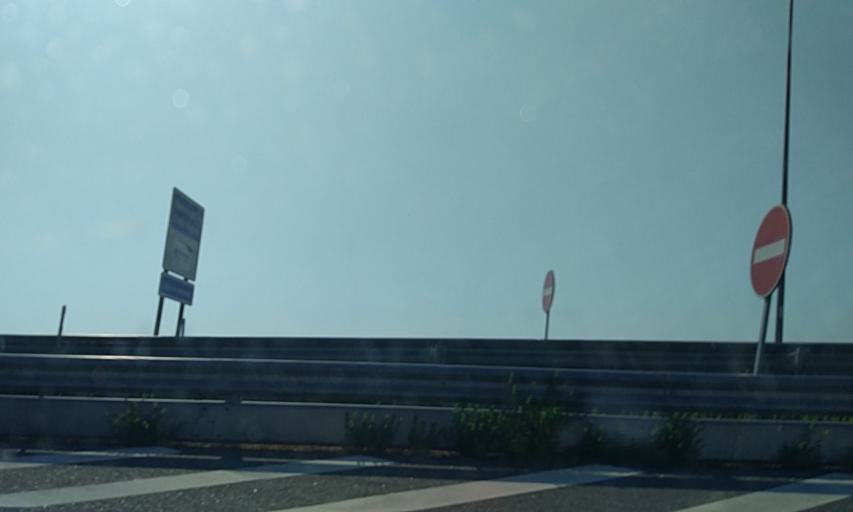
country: PT
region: Braganca
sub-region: Mirandela
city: Mirandela
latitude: 41.5102
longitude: -7.1814
